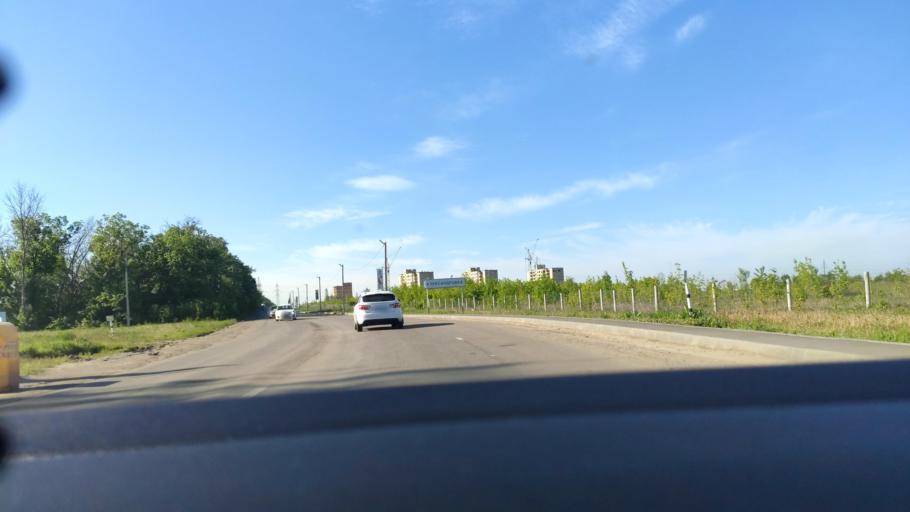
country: RU
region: Voronezj
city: Novaya Usman'
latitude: 51.6338
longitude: 39.3329
